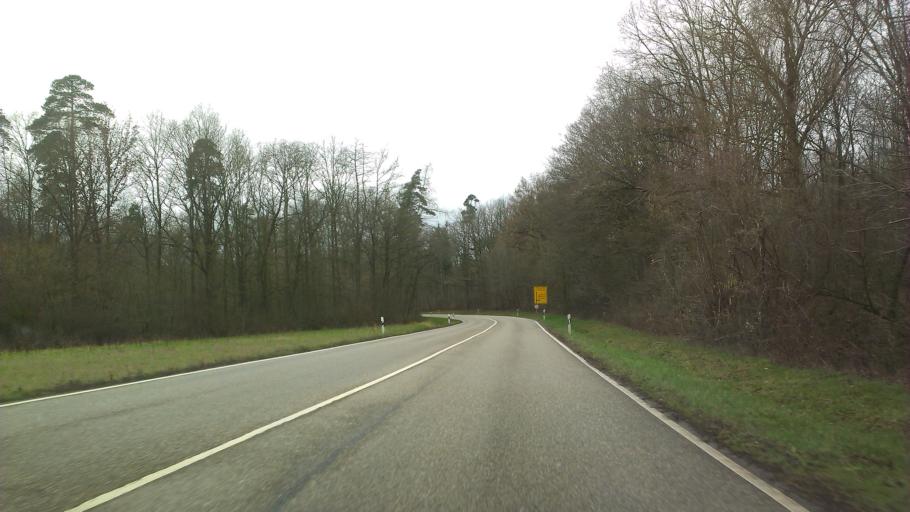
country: DE
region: Baden-Wuerttemberg
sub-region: Regierungsbezirk Stuttgart
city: Sersheim
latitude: 48.9569
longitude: 8.9900
